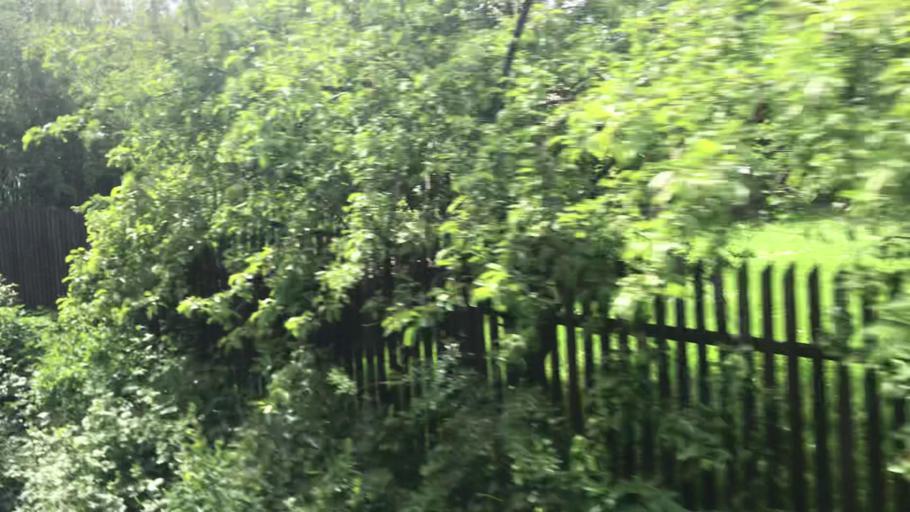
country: PL
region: Lower Silesian Voivodeship
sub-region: Powiat swidnicki
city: Swiebodzice
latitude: 50.8297
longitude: 16.3204
